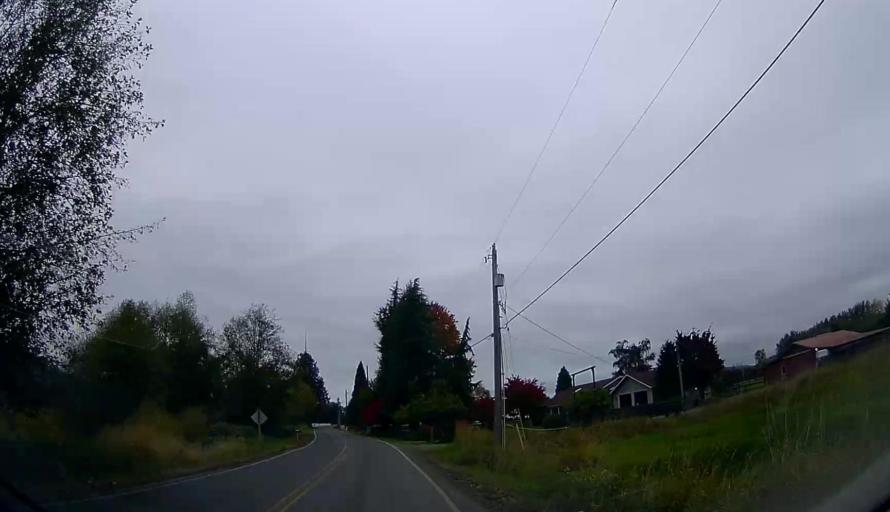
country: US
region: Washington
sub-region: Skagit County
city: Sedro-Woolley
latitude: 48.5051
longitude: -122.1909
